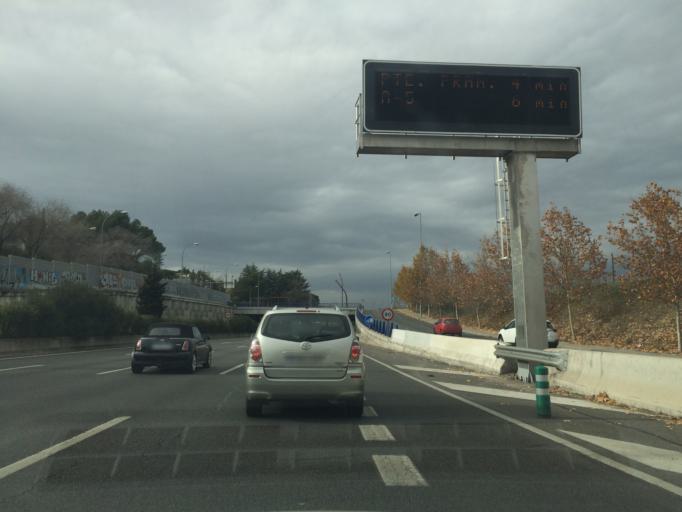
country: ES
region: Madrid
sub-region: Provincia de Madrid
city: Tetuan de las Victorias
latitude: 40.4728
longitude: -3.7329
